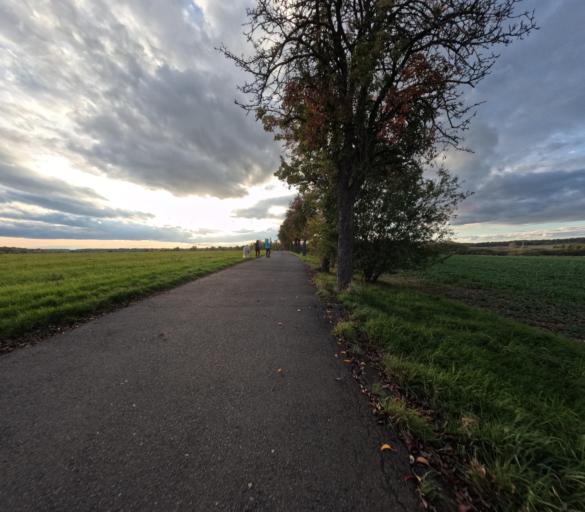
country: DE
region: Saxony
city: Grimma
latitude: 51.2418
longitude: 12.6920
